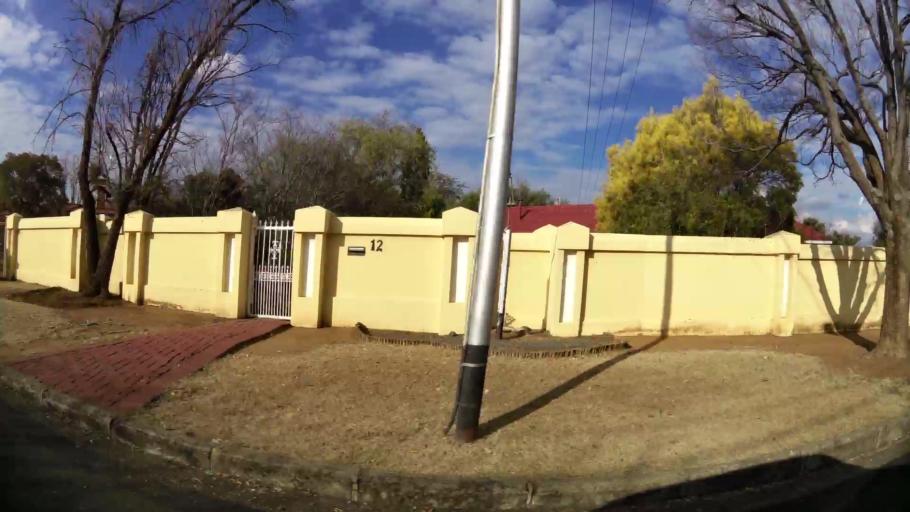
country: ZA
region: Orange Free State
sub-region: Mangaung Metropolitan Municipality
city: Bloemfontein
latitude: -29.0810
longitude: 26.2160
